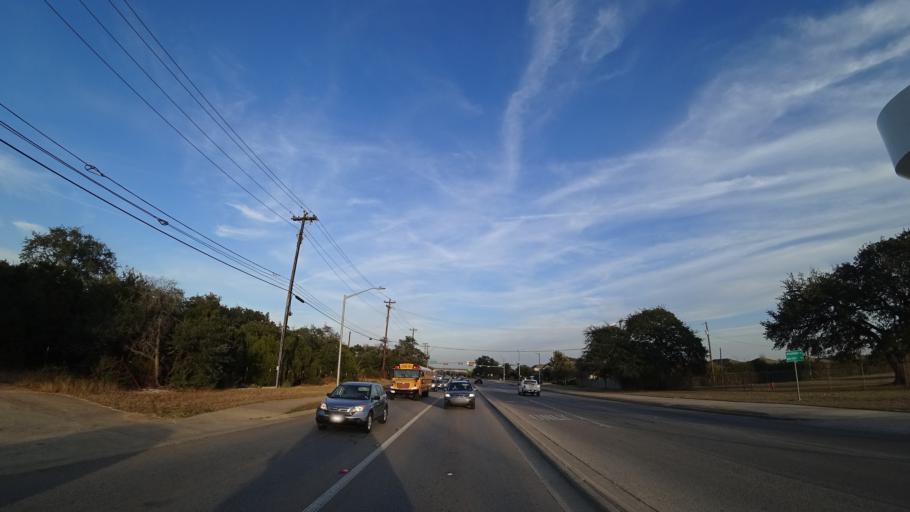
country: US
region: Texas
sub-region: Williamson County
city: Cedar Park
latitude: 30.5341
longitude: -97.8314
